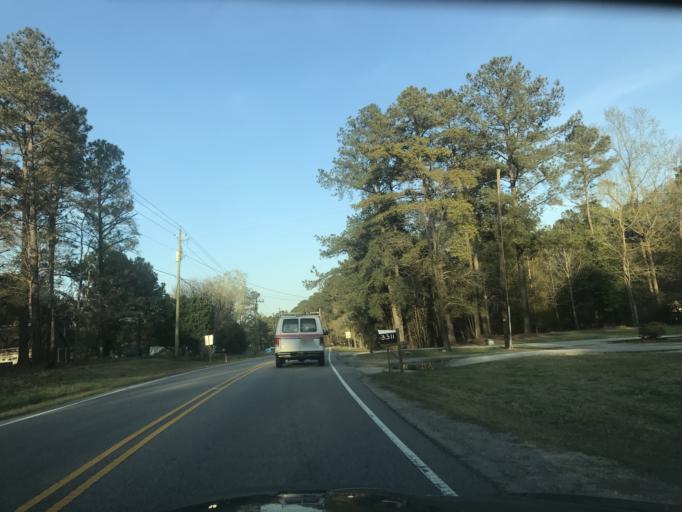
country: US
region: North Carolina
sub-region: Wake County
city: Garner
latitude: 35.7393
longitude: -78.5476
